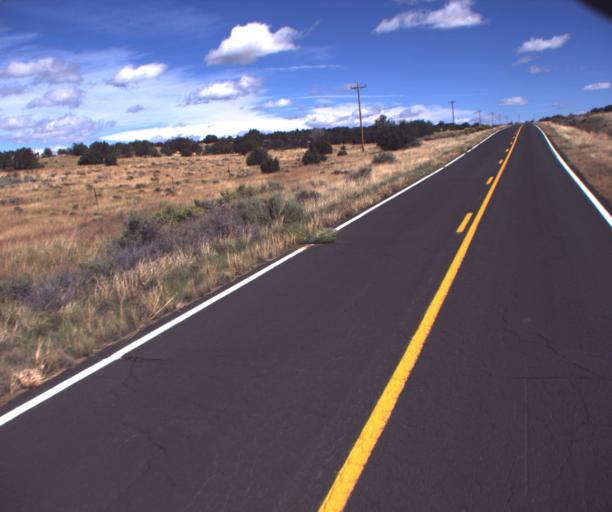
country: US
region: New Mexico
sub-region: McKinley County
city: Zuni Pueblo
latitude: 34.9837
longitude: -109.1237
